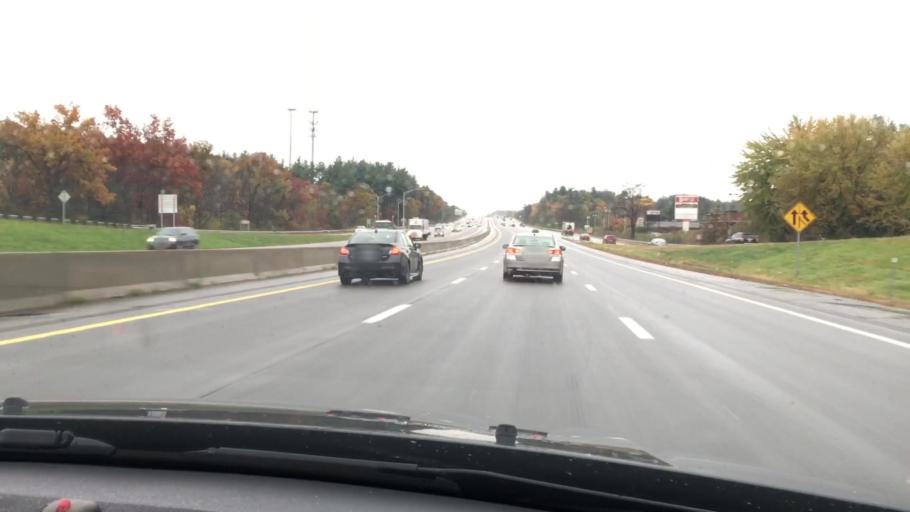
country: US
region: New Hampshire
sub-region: Hillsborough County
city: Nashua
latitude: 42.7680
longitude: -71.4937
